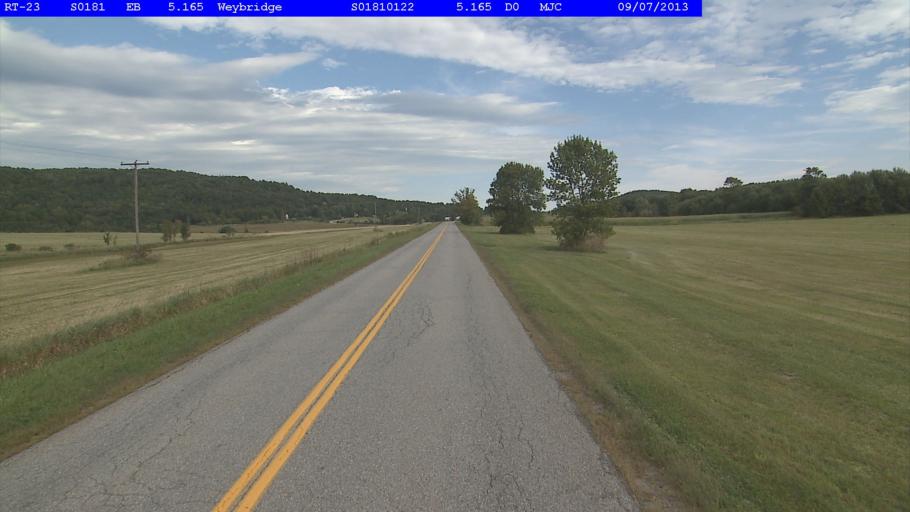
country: US
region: Vermont
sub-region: Addison County
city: Middlebury (village)
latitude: 44.0654
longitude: -73.2498
